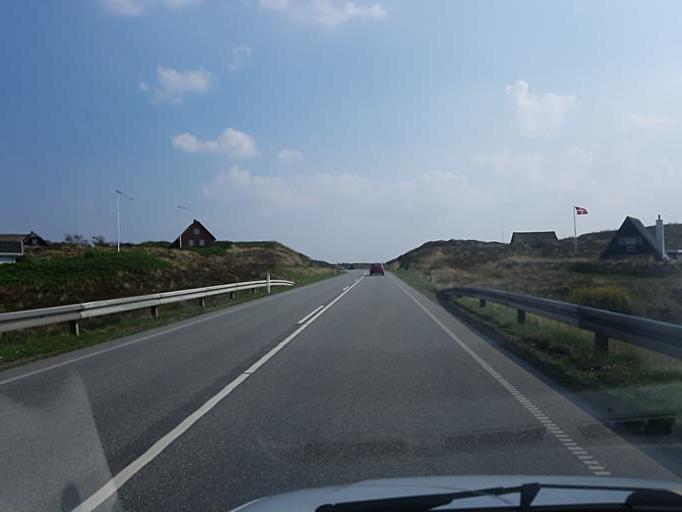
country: DK
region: Central Jutland
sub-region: Ringkobing-Skjern Kommune
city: Hvide Sande
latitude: 55.9044
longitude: 8.1667
